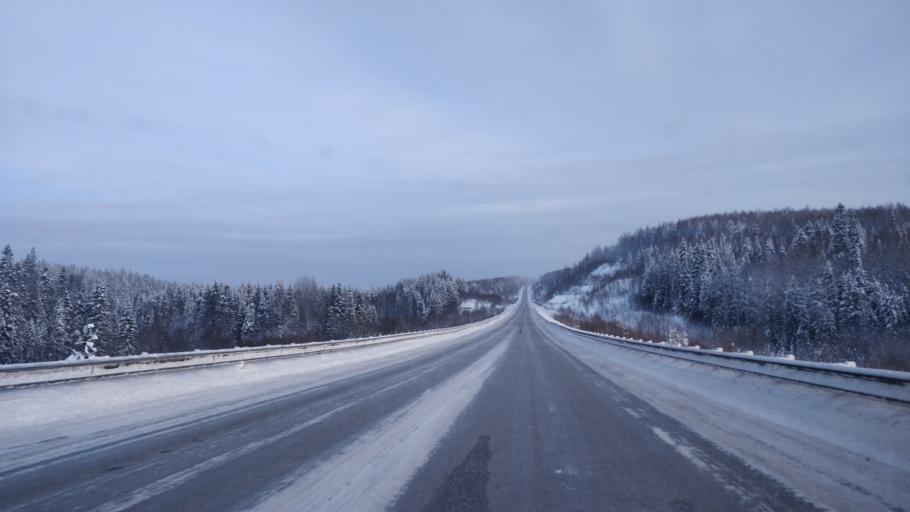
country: RU
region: Perm
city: Polazna
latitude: 58.2908
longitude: 56.5117
